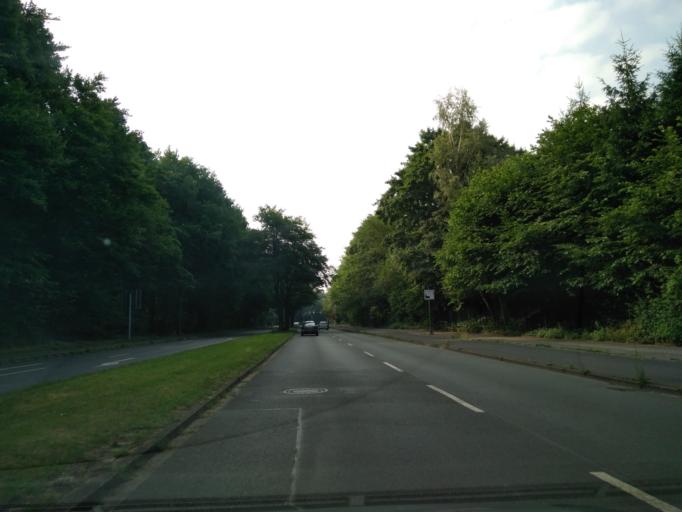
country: DE
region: North Rhine-Westphalia
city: Marl
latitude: 51.5856
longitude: 7.0638
